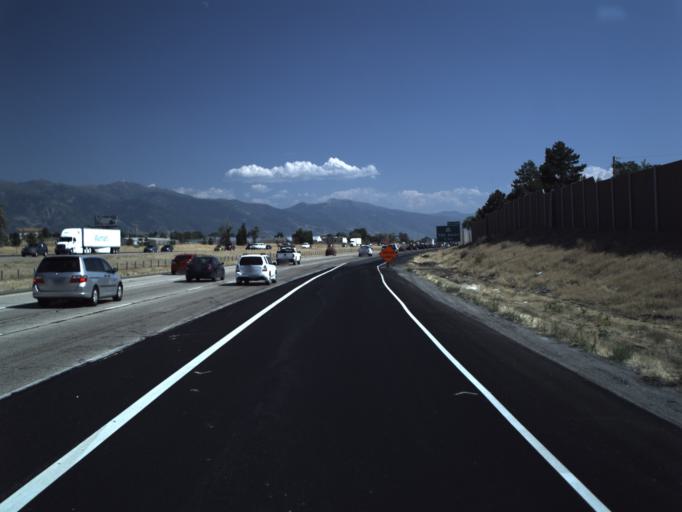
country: US
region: Utah
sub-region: Davis County
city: Clearfield
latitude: 41.1201
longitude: -112.0198
